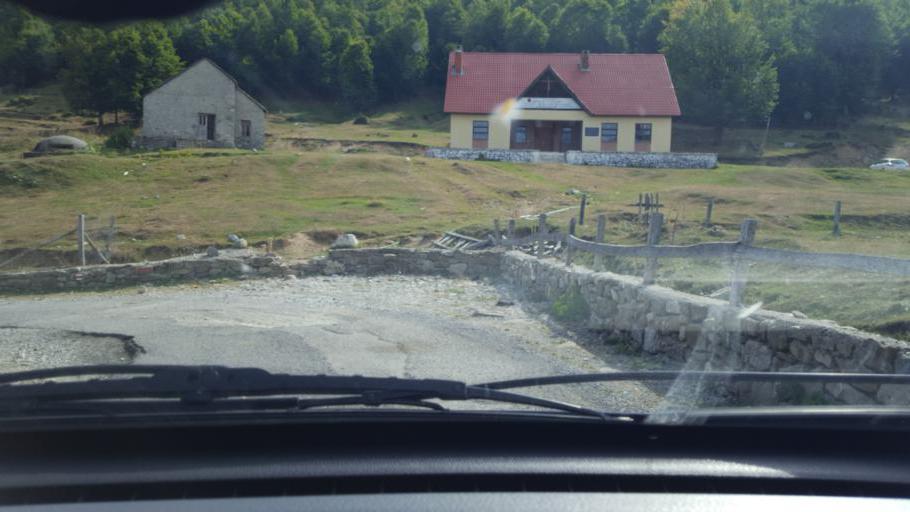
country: AL
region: Kukes
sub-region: Rrethi i Tropojes
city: Valbone
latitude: 42.5319
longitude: 19.7188
